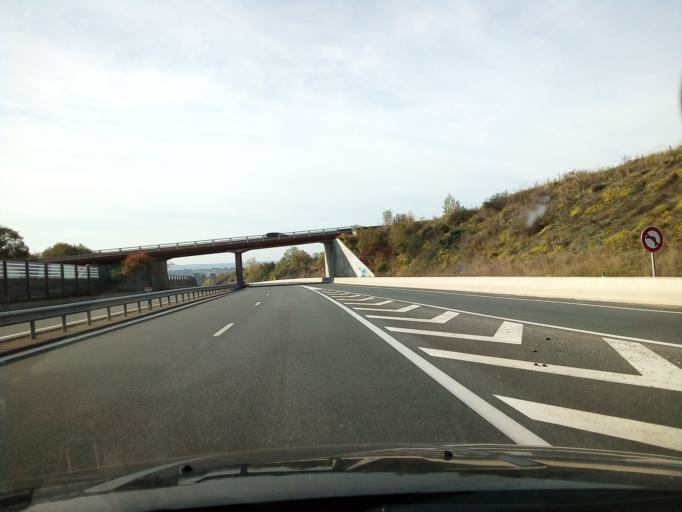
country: FR
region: Auvergne
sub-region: Departement de l'Allier
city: Saint-Victor
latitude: 46.3805
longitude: 2.6184
